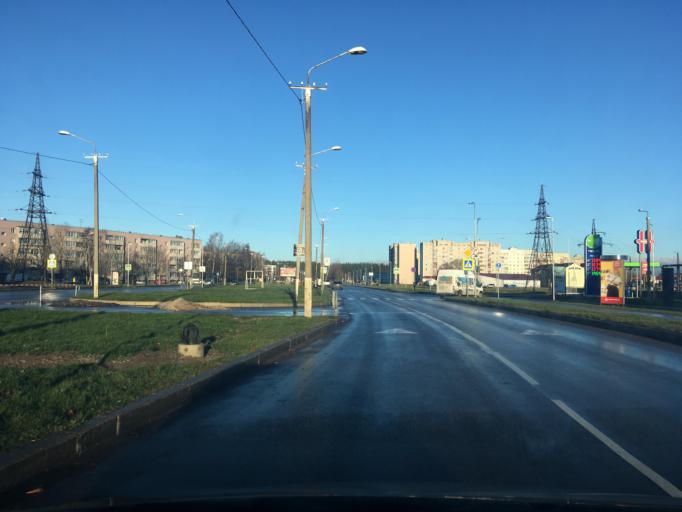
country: EE
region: Ida-Virumaa
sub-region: Narva linn
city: Narva
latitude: 59.3864
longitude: 28.1763
